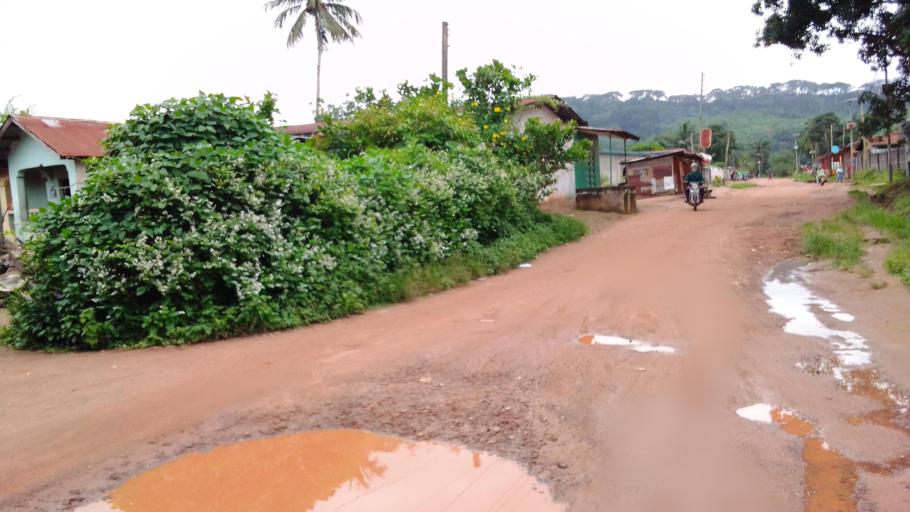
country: SL
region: Eastern Province
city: Kenema
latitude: 7.8586
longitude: -11.2038
